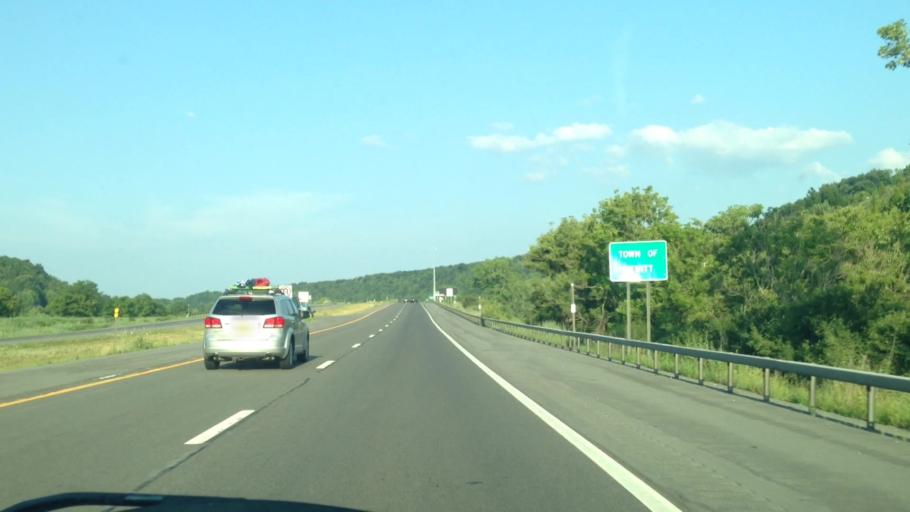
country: US
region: New York
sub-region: Onondaga County
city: Nedrow
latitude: 43.0048
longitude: -76.1090
